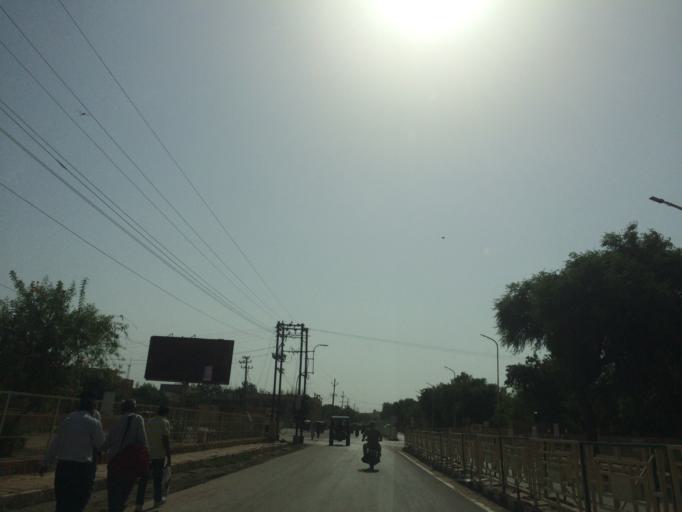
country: IN
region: Rajasthan
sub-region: Jaisalmer
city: Jaisalmer
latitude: 26.9158
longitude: 70.9036
